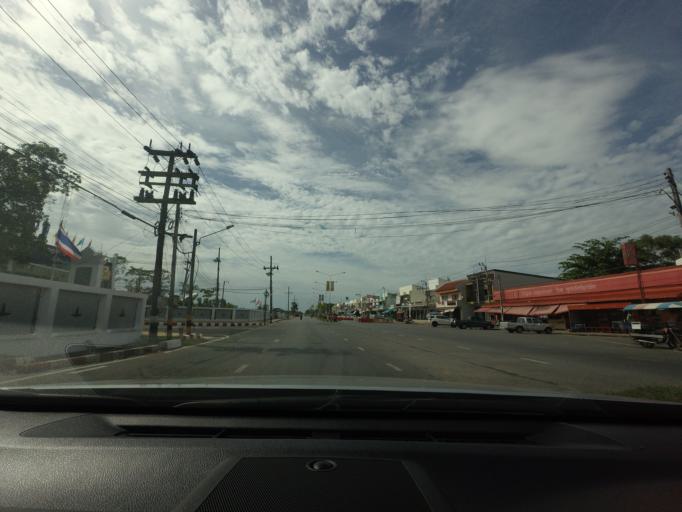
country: TH
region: Songkhla
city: Khlong Hoi Khong
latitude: 6.9303
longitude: 100.4160
